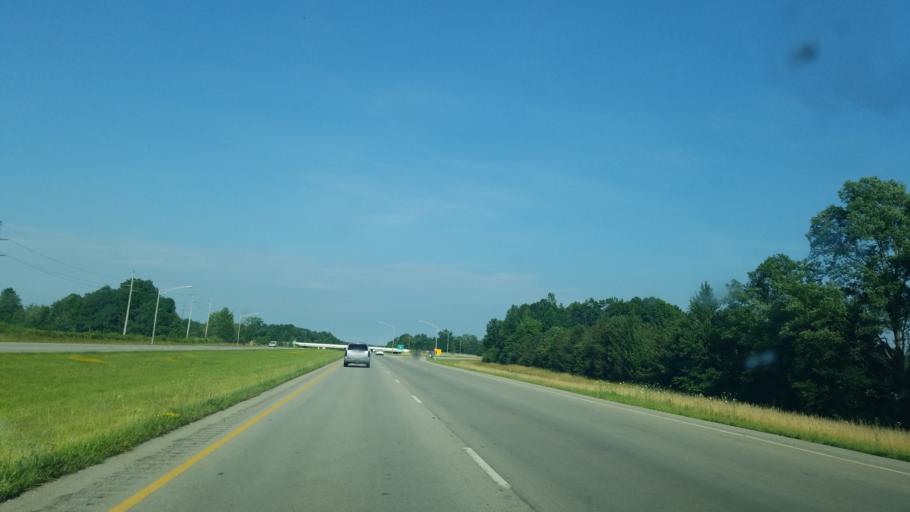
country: US
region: Ohio
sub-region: Clermont County
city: Williamsburg
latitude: 39.0671
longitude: -84.0675
